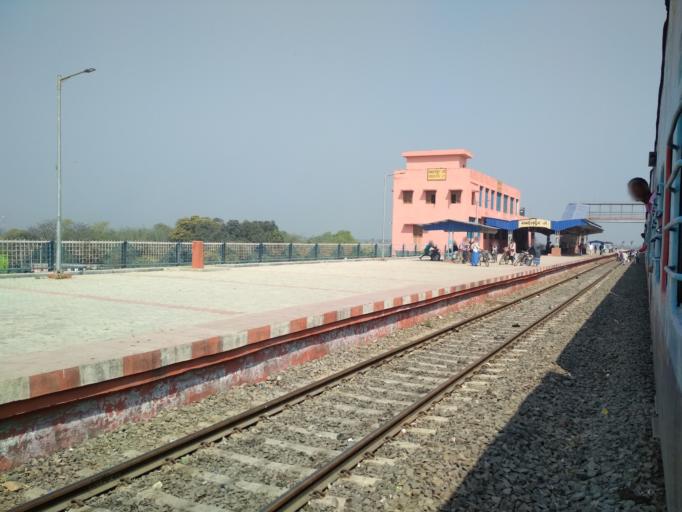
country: IN
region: Bihar
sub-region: Munger
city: Munger
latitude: 25.4270
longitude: 86.4388
